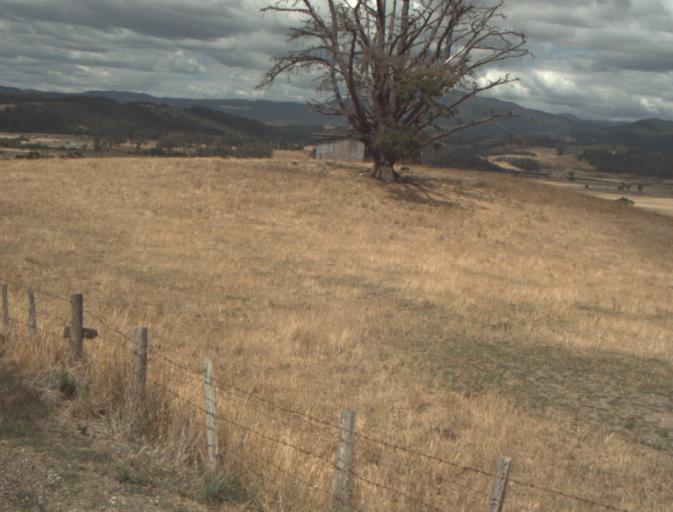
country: AU
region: Tasmania
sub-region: Launceston
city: Mayfield
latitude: -41.2271
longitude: 147.1163
